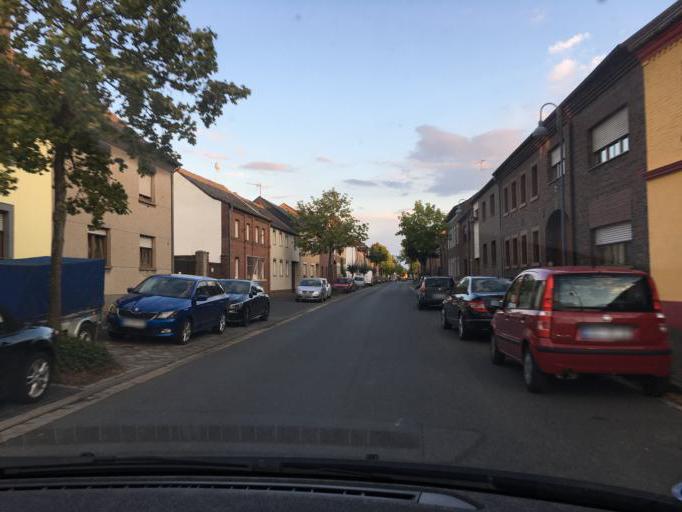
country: DE
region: North Rhine-Westphalia
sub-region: Regierungsbezirk Koln
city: Niederzier
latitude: 50.8571
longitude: 6.4568
